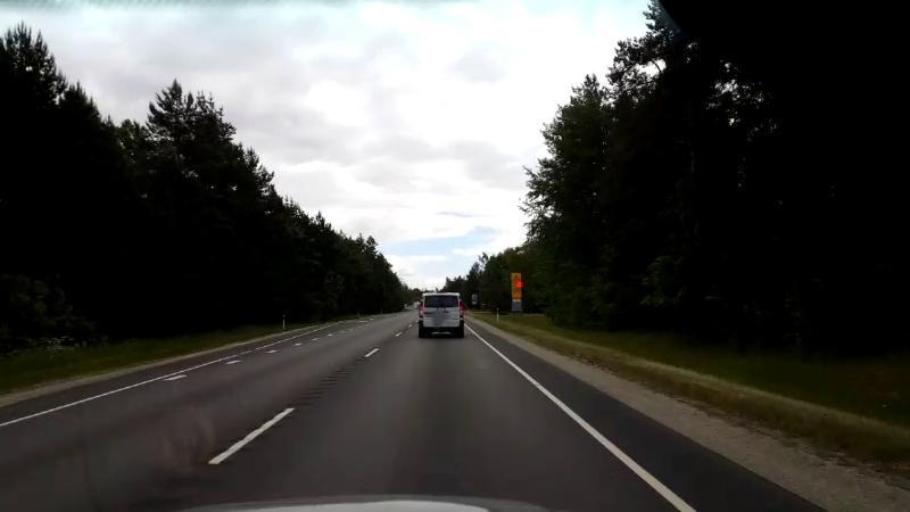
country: EE
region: Paernumaa
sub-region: Paernu linn
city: Parnu
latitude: 58.2087
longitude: 24.4852
